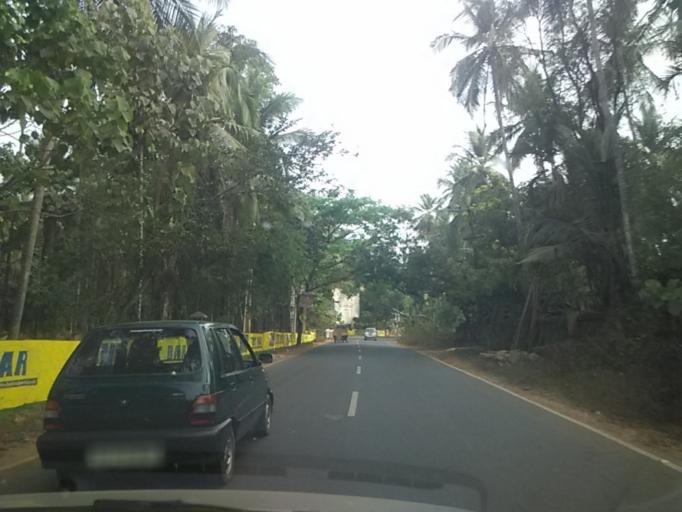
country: IN
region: Kerala
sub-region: Kozhikode
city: Naduvannur
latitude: 11.4951
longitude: 75.7744
